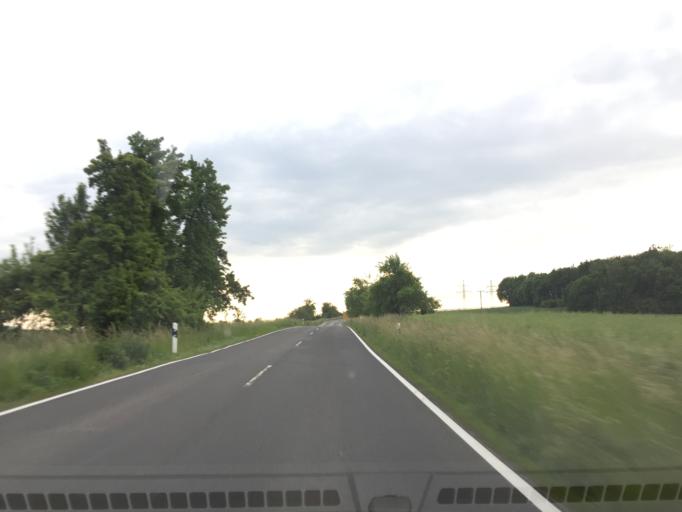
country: DE
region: Rheinland-Pfalz
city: Hundsangen
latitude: 50.4492
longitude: 7.9825
